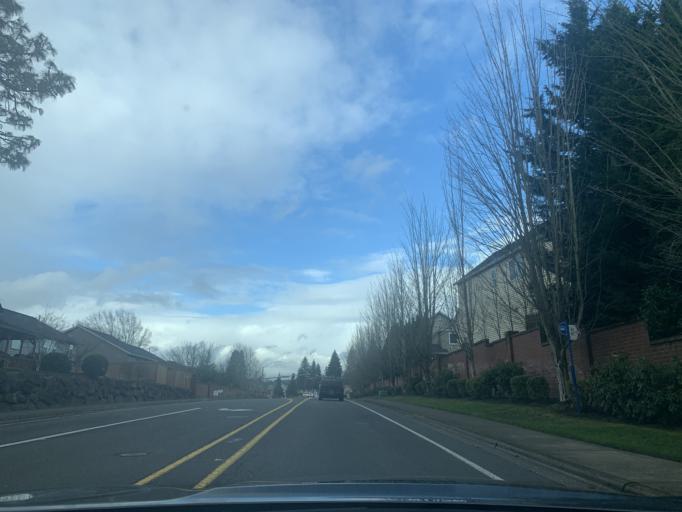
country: US
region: Oregon
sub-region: Washington County
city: Oak Hills
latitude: 45.5650
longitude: -122.8356
